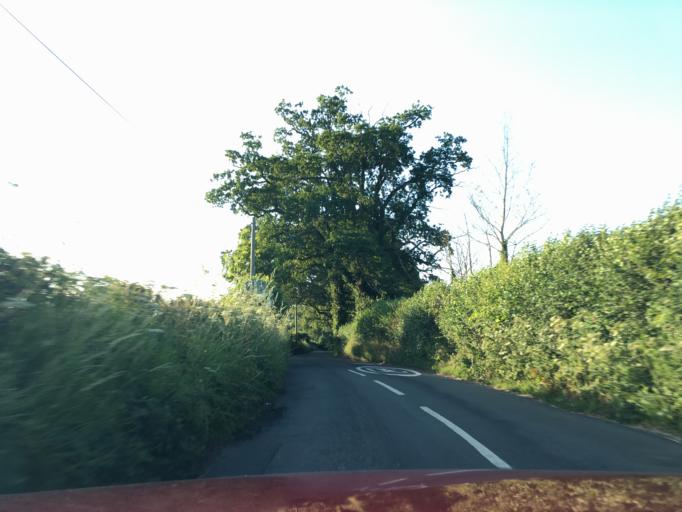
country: GB
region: England
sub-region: Hampshire
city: Tadley
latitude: 51.4182
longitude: -1.1627
